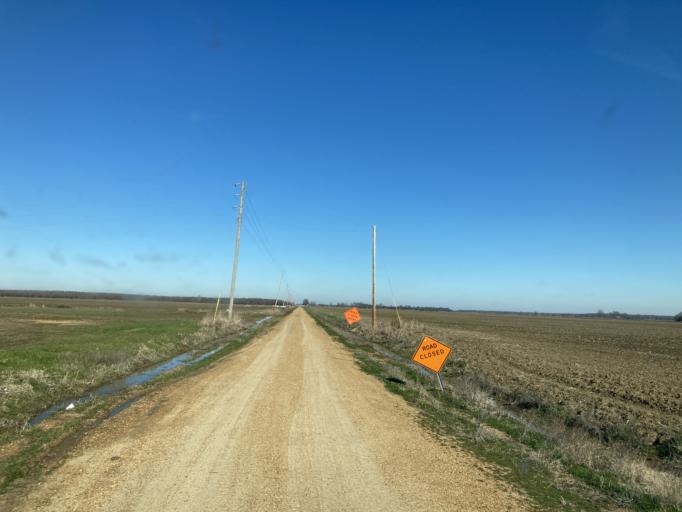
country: US
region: Mississippi
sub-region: Humphreys County
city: Belzoni
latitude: 32.9811
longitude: -90.6223
